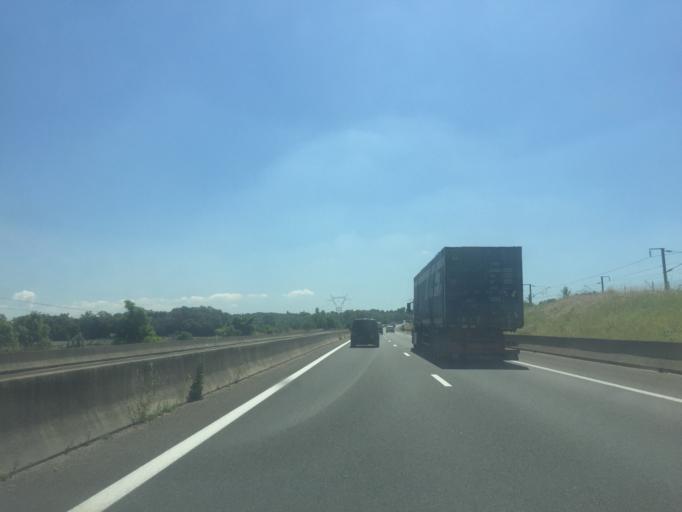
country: FR
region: Rhone-Alpes
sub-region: Departement du Rhone
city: Jonage
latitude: 45.8150
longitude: 5.0536
